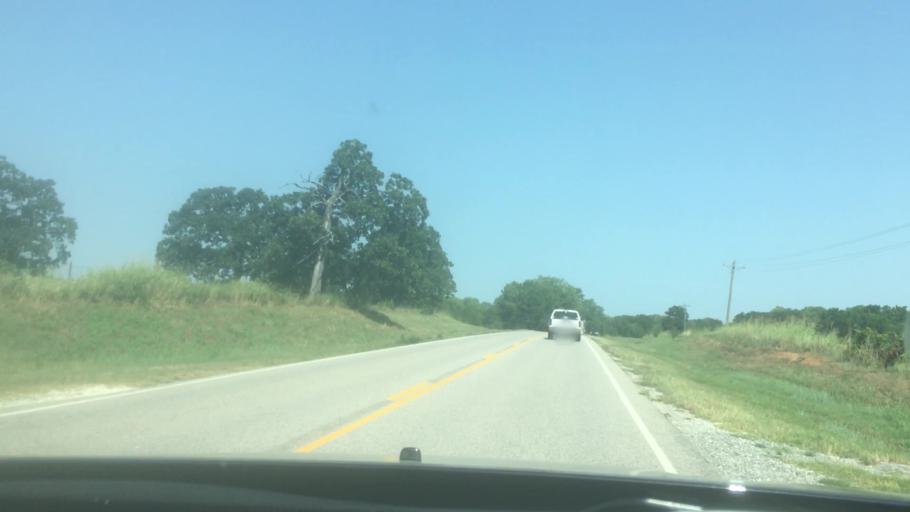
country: US
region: Oklahoma
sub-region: Bryan County
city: Durant
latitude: 34.1726
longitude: -96.4116
